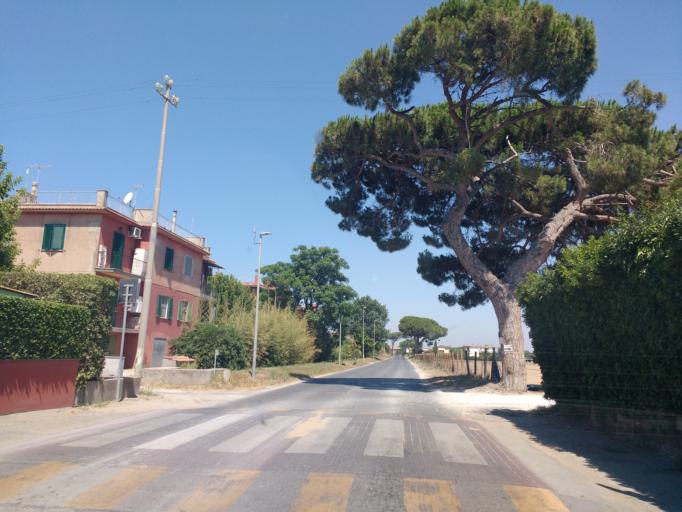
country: IT
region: Latium
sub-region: Citta metropolitana di Roma Capitale
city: Fregene
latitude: 41.8468
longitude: 12.2212
